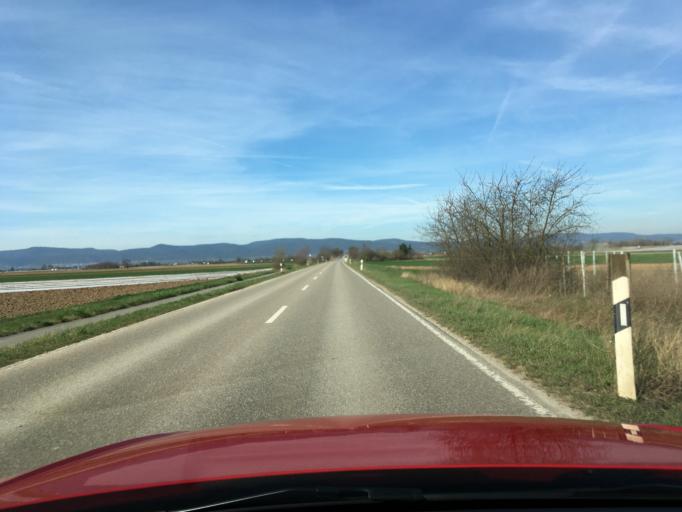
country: DE
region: Rheinland-Pfalz
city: Bohl-Iggelheim
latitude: 49.3902
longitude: 8.2830
